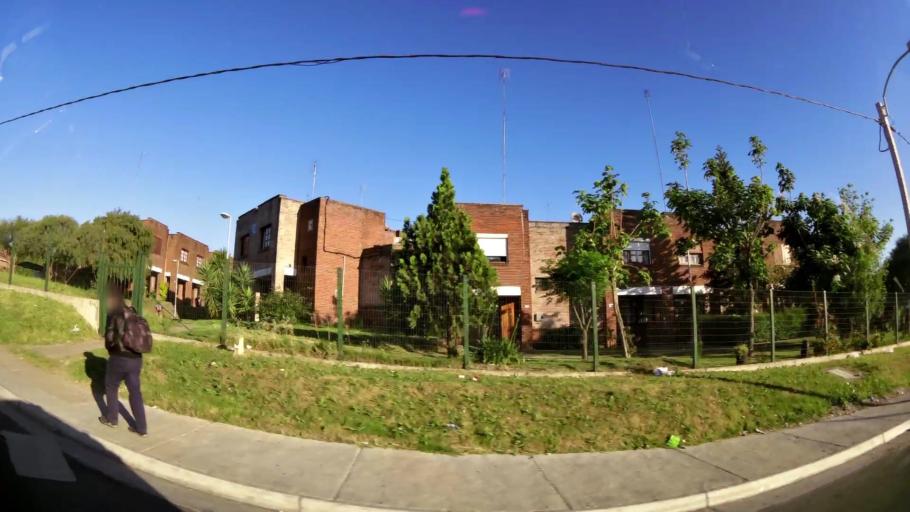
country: UY
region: Canelones
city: La Paz
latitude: -34.8312
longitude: -56.2317
